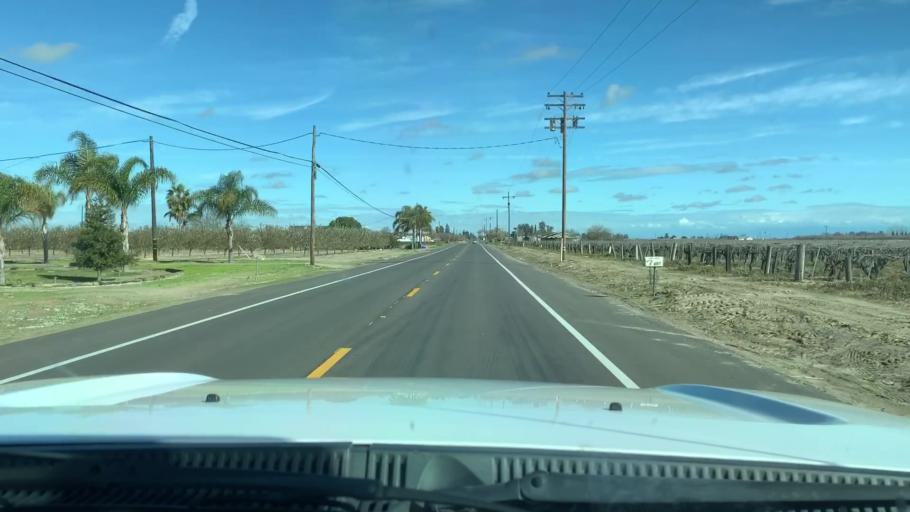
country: US
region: California
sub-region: Fresno County
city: Selma
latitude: 36.5379
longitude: -119.6828
